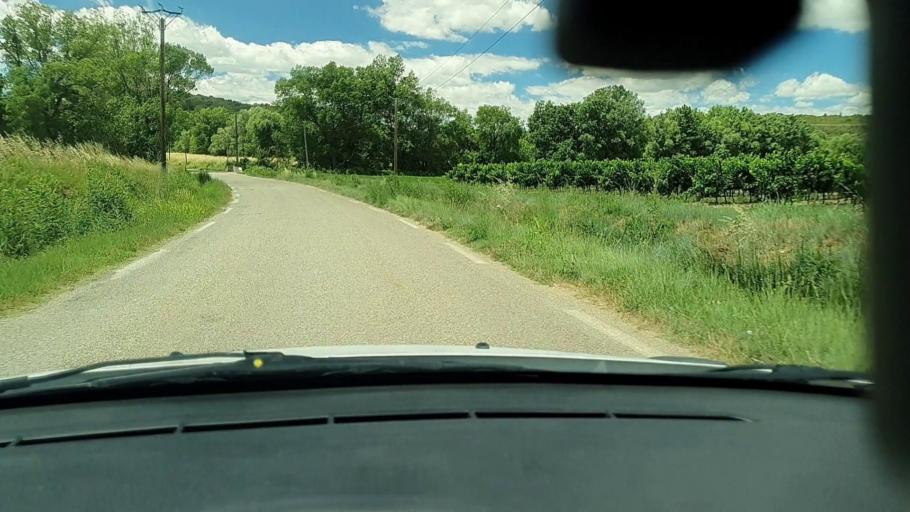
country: FR
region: Languedoc-Roussillon
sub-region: Departement du Gard
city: Blauzac
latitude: 43.9498
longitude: 4.3849
